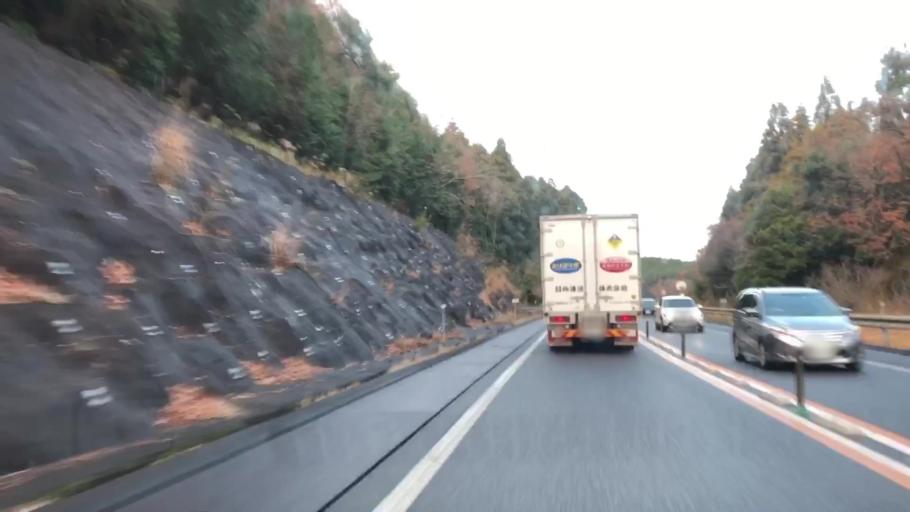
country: JP
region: Saga Prefecture
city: Imaricho-ko
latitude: 33.1560
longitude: 129.8760
